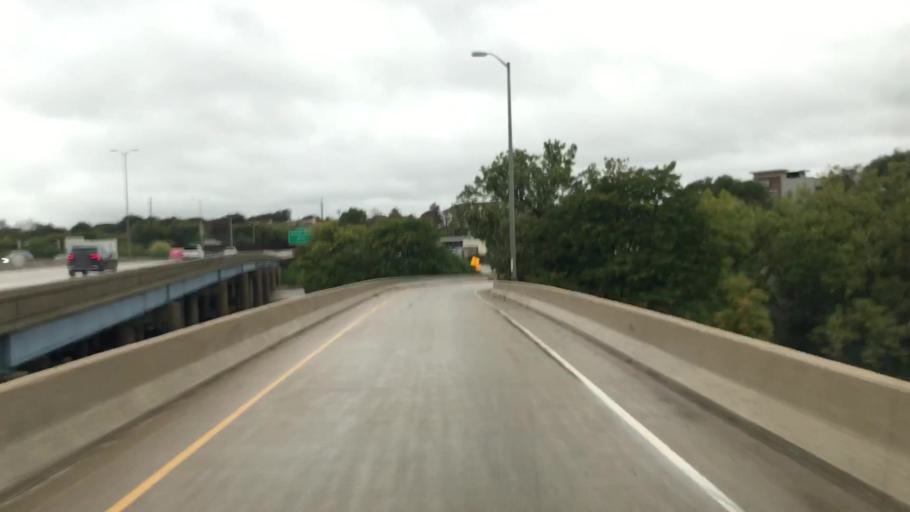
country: US
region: Wisconsin
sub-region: Waukesha County
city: Elm Grove
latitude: 43.0553
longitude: -88.0459
